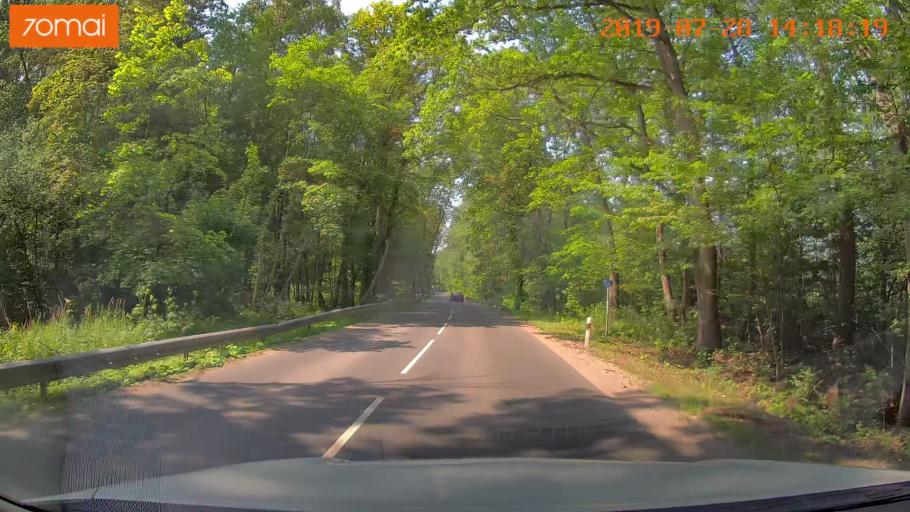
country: RU
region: Kaliningrad
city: Volochayevskoye
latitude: 54.8168
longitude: 20.2422
